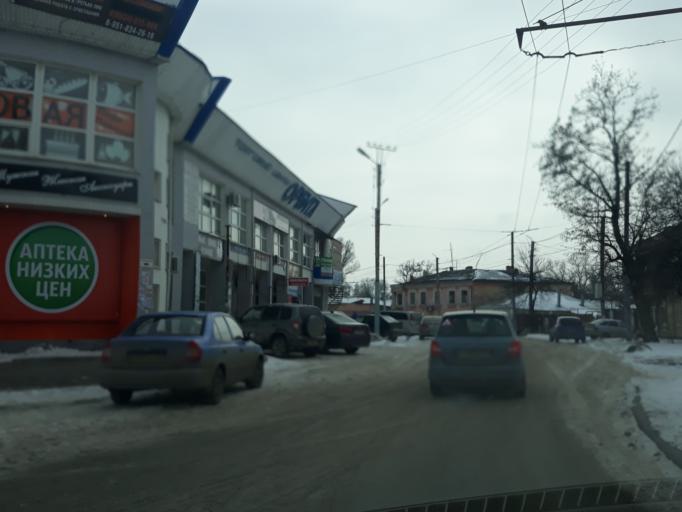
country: RU
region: Rostov
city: Taganrog
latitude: 47.2130
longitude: 38.9145
